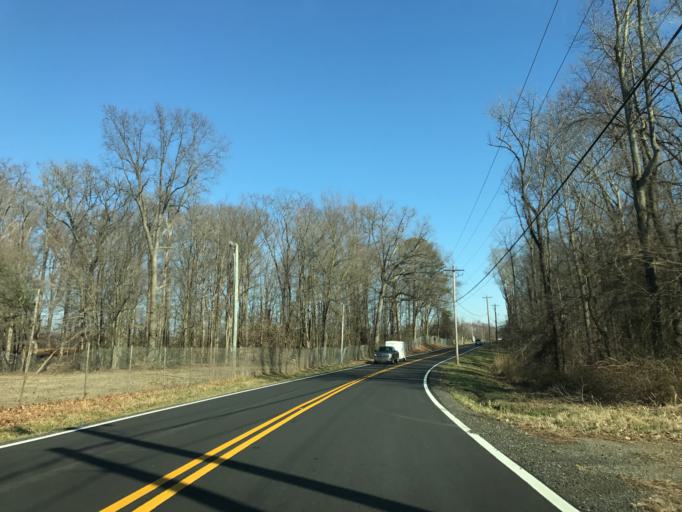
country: US
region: Maryland
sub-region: Queen Anne's County
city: Centreville
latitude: 39.0279
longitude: -76.1154
